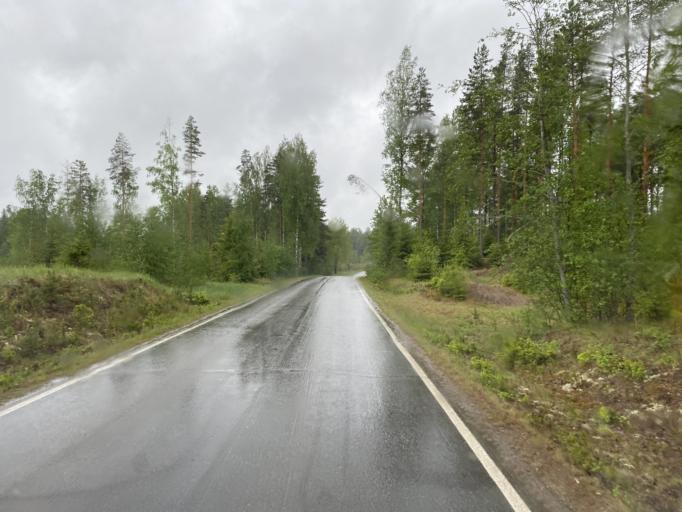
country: FI
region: Haeme
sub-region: Forssa
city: Humppila
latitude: 61.0810
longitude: 23.3116
